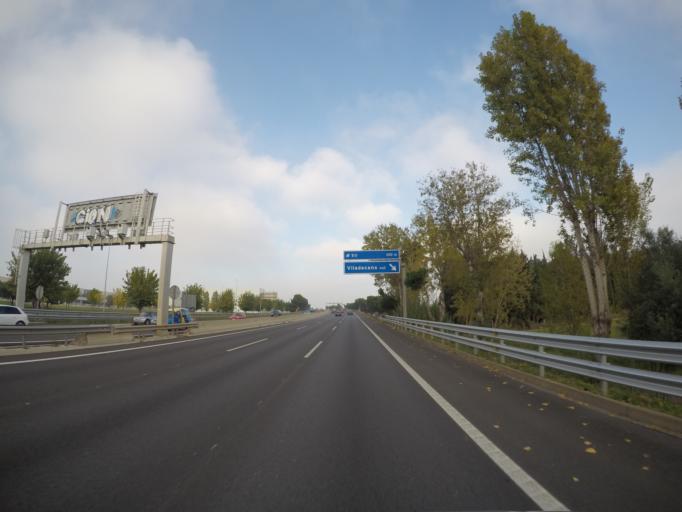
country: ES
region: Catalonia
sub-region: Provincia de Barcelona
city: Viladecans
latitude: 41.2977
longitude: 2.0184
